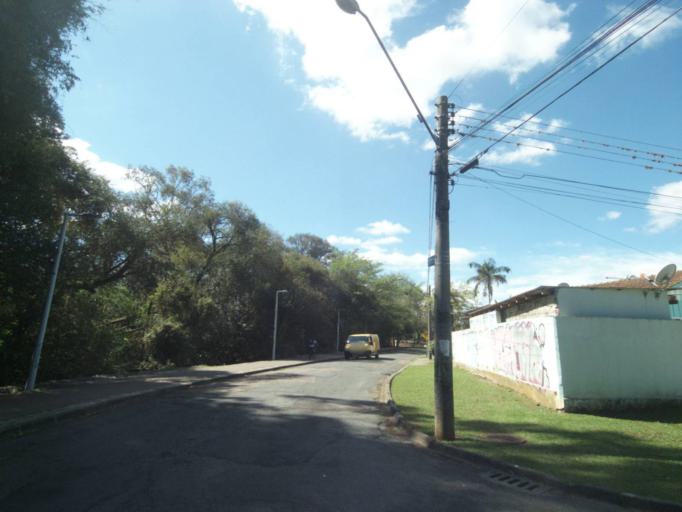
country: BR
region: Parana
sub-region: Curitiba
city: Curitiba
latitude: -25.3955
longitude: -49.2700
